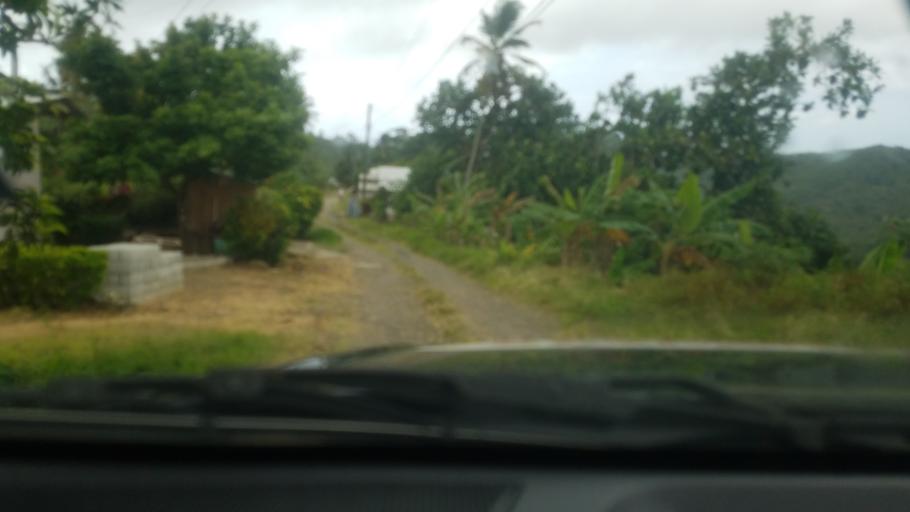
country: LC
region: Micoud Quarter
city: Micoud
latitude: 13.8029
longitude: -60.9464
